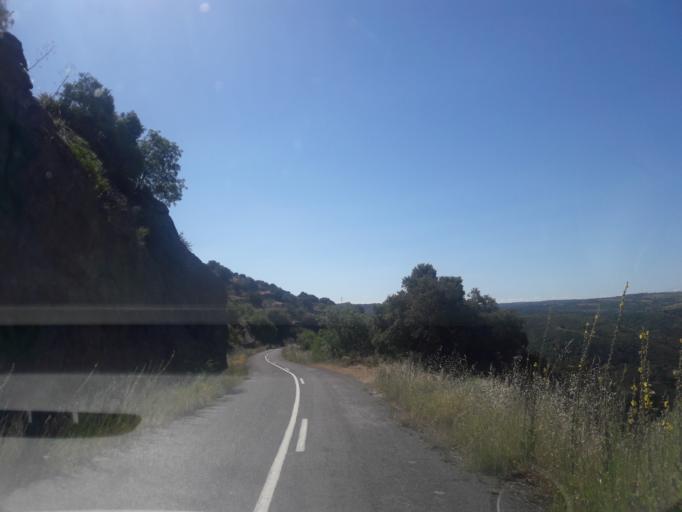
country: ES
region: Castille and Leon
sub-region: Provincia de Salamanca
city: Saucelle
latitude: 41.0321
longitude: -6.7591
